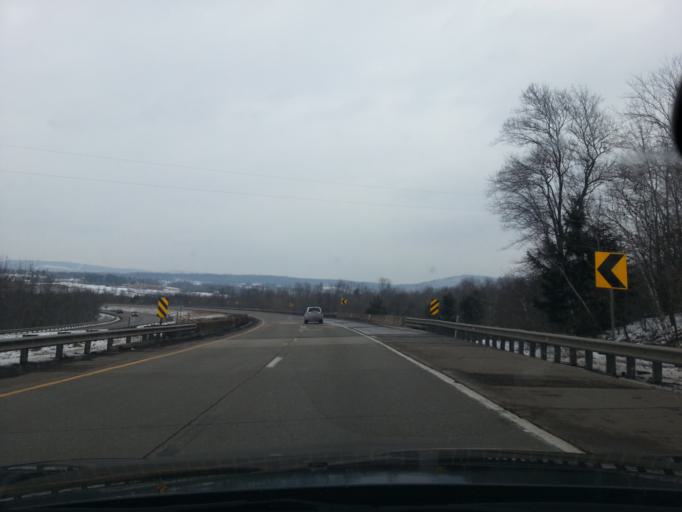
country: US
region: Pennsylvania
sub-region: Luzerne County
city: Harleigh
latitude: 40.9994
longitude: -76.0086
